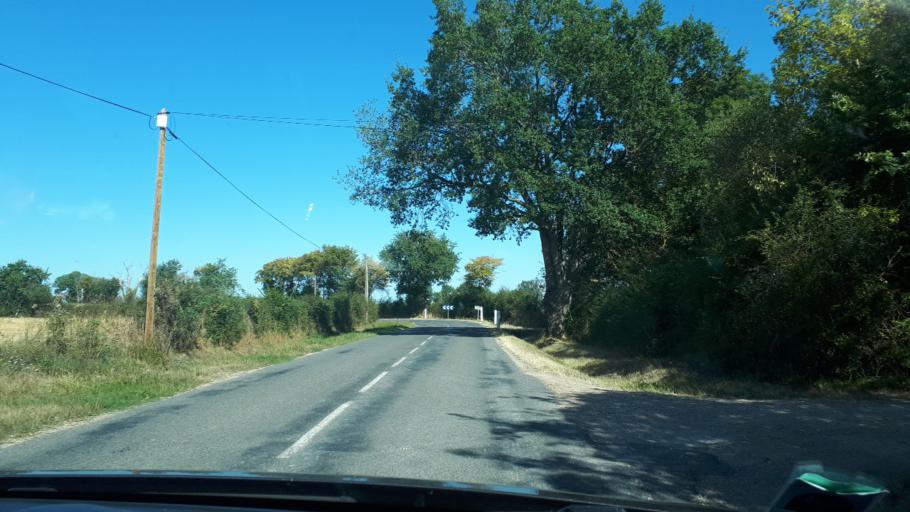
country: FR
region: Centre
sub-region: Departement du Loiret
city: Briare
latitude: 47.5895
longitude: 2.7281
